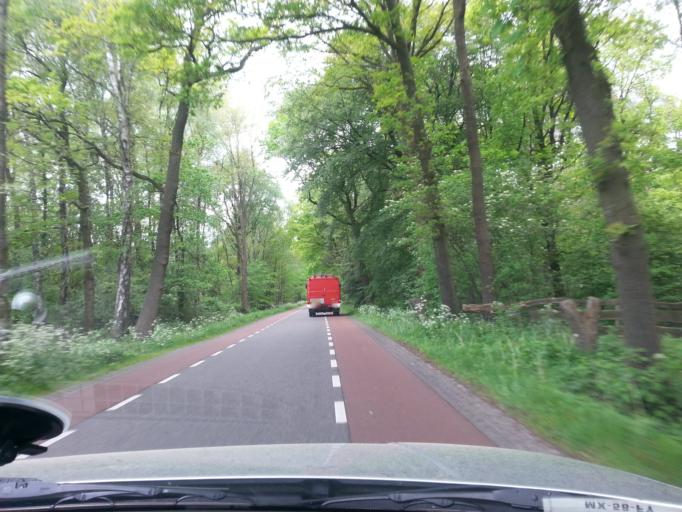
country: NL
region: Overijssel
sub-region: Gemeente Losser
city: Losser
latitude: 52.2890
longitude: 6.9986
